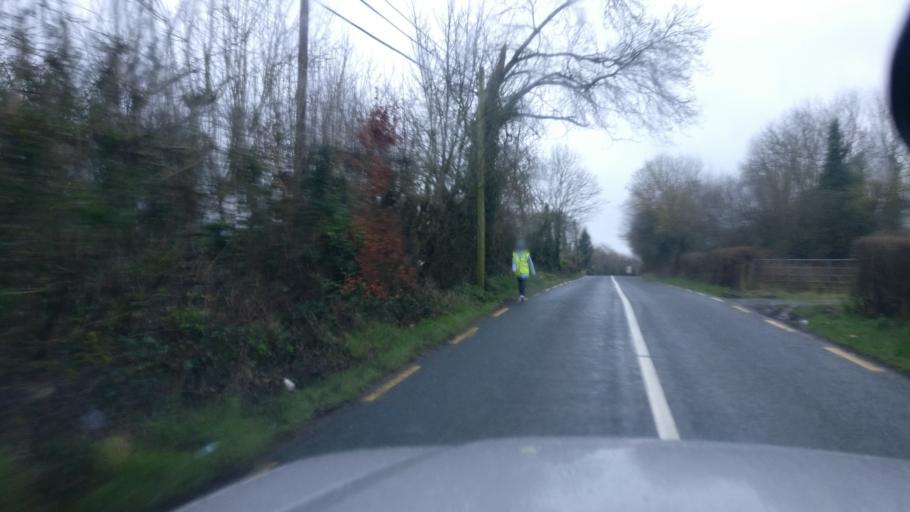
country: IE
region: Connaught
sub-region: County Galway
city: Ballinasloe
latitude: 53.2235
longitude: -8.1942
